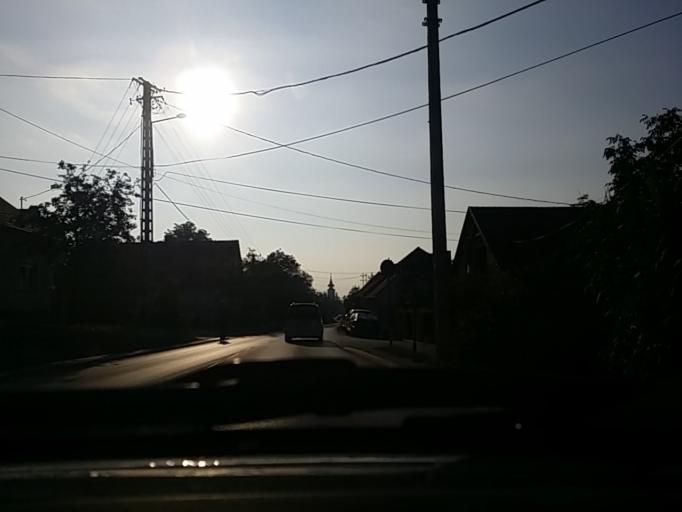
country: HU
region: Pest
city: Szentendre
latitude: 47.6791
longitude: 19.0573
